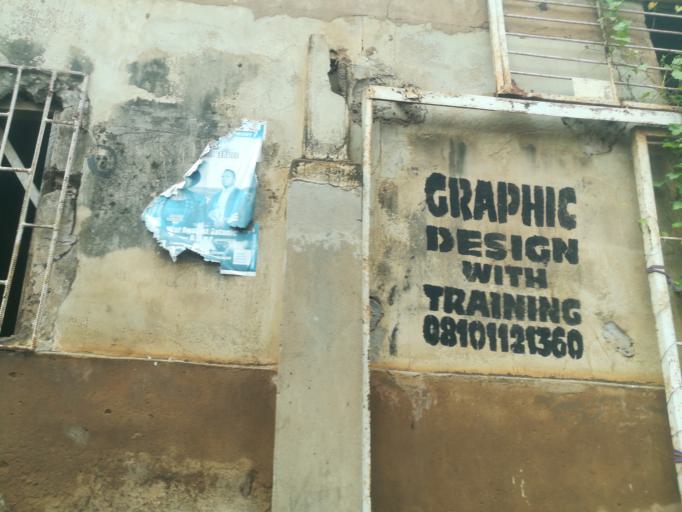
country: NG
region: Oyo
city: Ibadan
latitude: 7.3548
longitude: 3.8779
